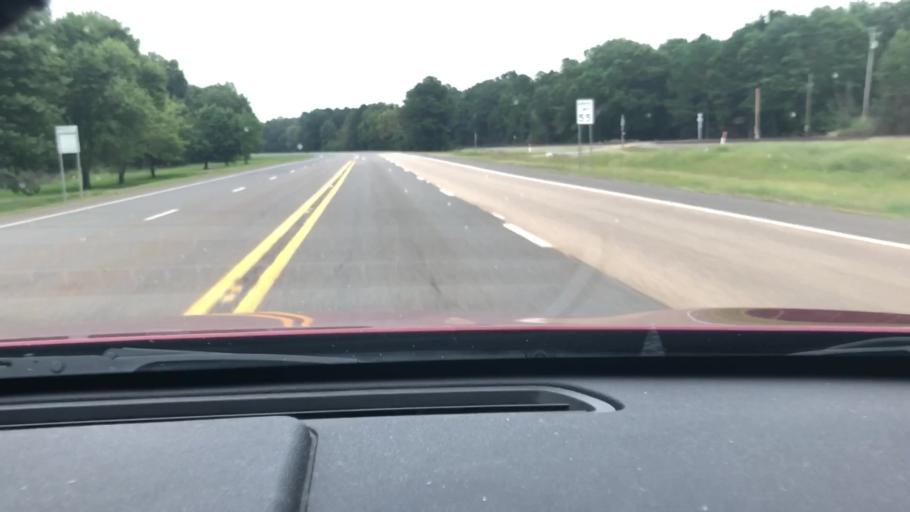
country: US
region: Arkansas
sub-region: Lafayette County
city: Lewisville
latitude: 33.3551
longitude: -93.5720
